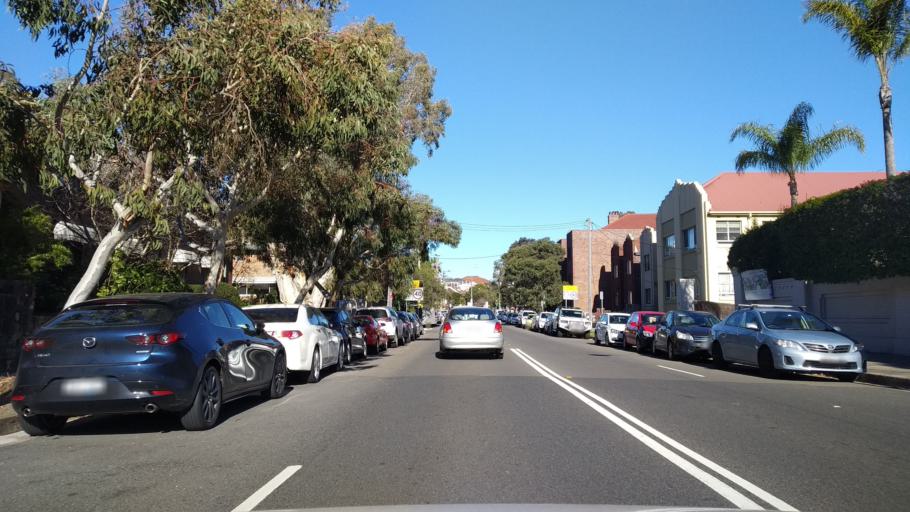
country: AU
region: New South Wales
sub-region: Waverley
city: Bondi Junction
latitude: -33.8965
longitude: 151.2514
